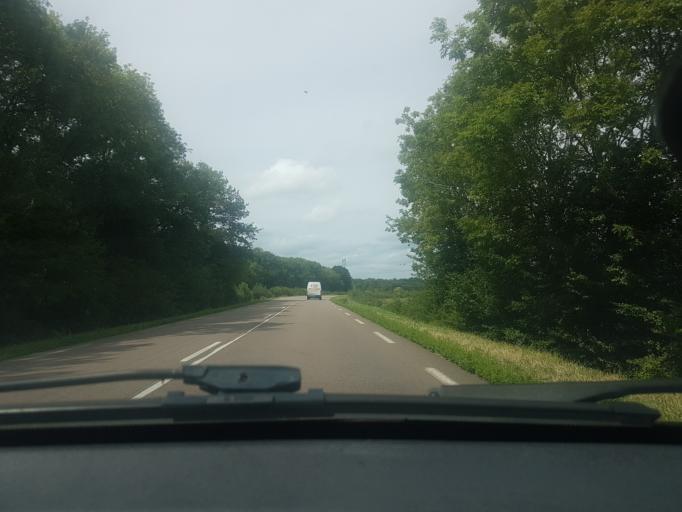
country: FR
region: Bourgogne
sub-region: Departement de la Cote-d'Or
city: Nolay
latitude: 47.0385
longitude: 4.6189
